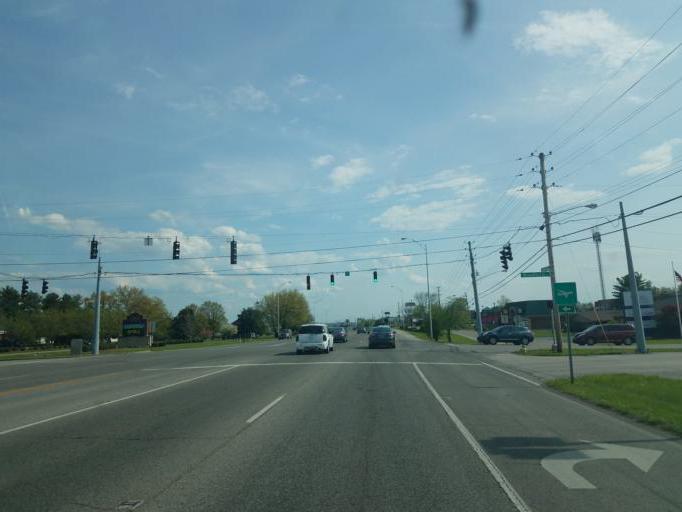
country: US
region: Kentucky
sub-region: Warren County
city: Bowling Green
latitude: 36.9645
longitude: -86.4316
